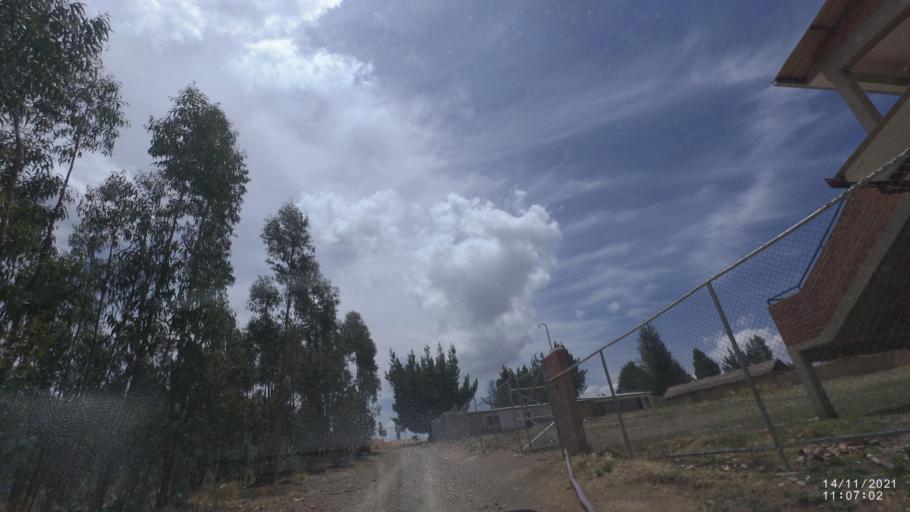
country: BO
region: Cochabamba
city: Cochabamba
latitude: -17.3330
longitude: -66.0545
